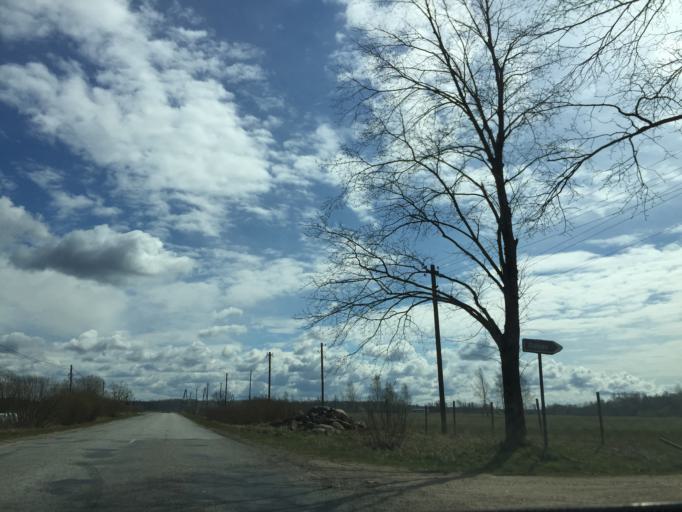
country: LV
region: Salacgrivas
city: Salacgriva
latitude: 57.7451
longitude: 24.3914
